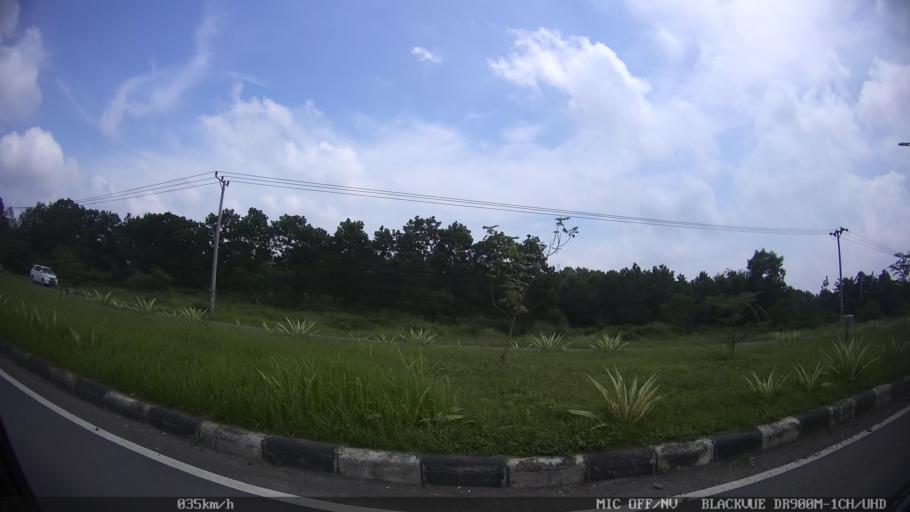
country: ID
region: Lampung
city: Kedaton
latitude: -5.3575
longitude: 105.3122
